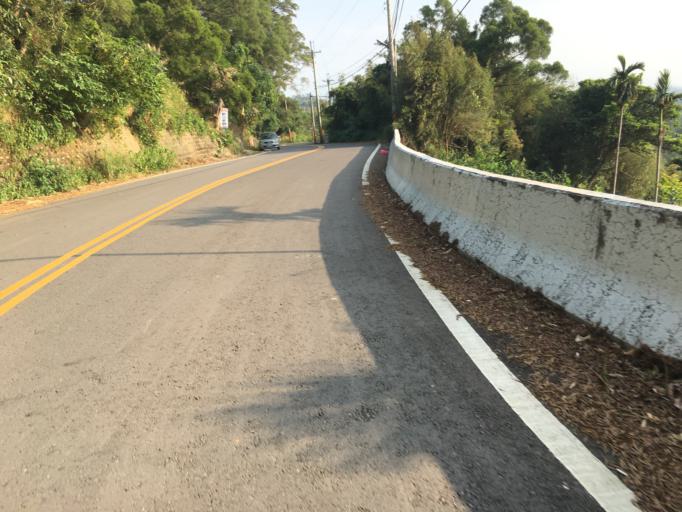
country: TW
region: Taiwan
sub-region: Hsinchu
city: Hsinchu
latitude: 24.7521
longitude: 121.0316
